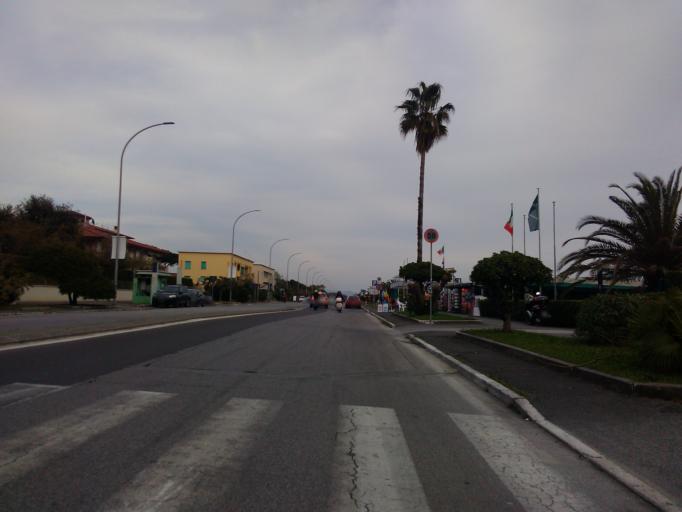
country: IT
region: Tuscany
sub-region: Provincia di Massa-Carrara
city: Massa
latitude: 44.0023
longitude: 10.1080
